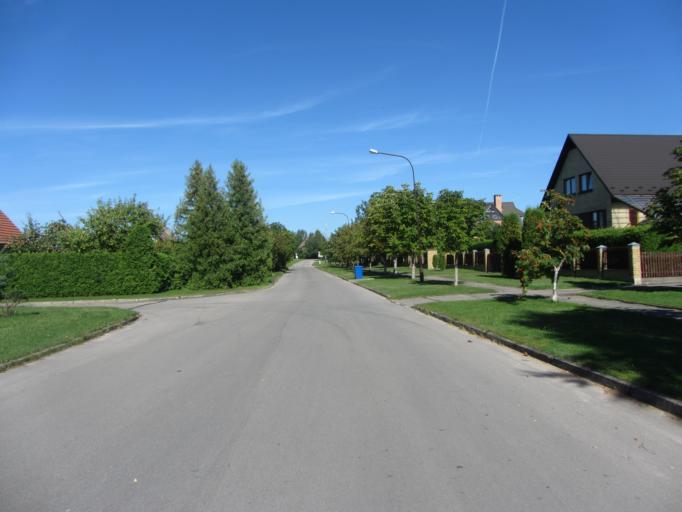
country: LT
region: Alytaus apskritis
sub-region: Alytus
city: Alytus
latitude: 54.4402
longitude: 23.9928
